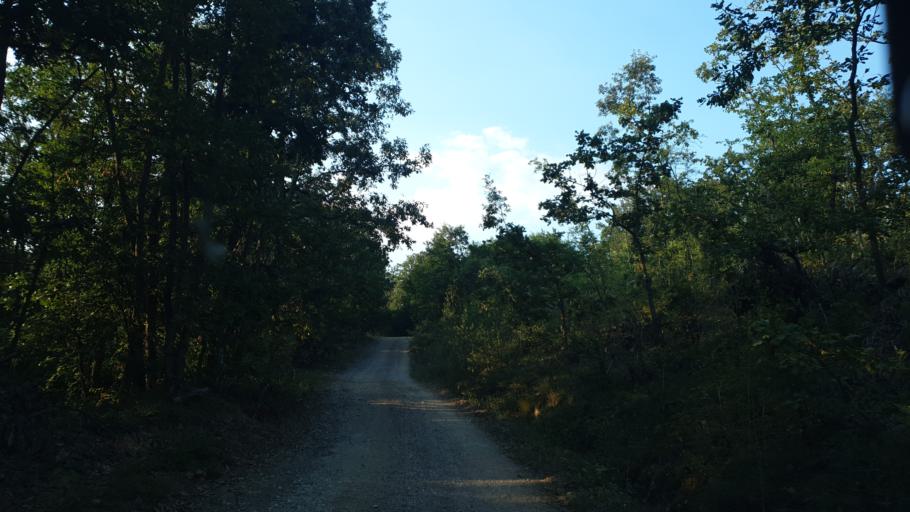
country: RS
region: Central Serbia
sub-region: Zlatiborski Okrug
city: Kosjeric
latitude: 44.0006
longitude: 20.0031
